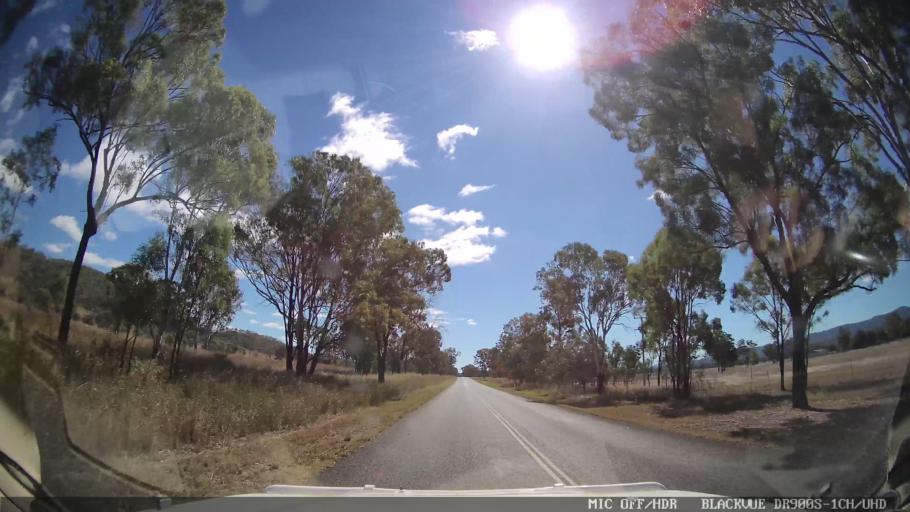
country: AU
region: Queensland
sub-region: Gladstone
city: Toolooa
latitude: -24.4526
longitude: 151.3462
